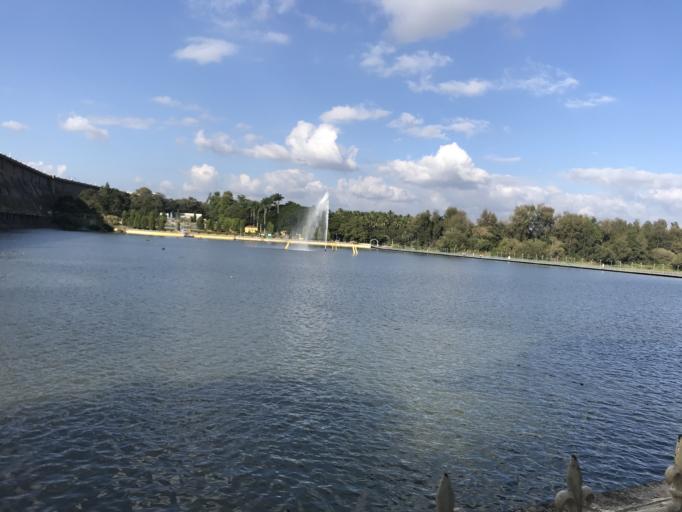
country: IN
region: Karnataka
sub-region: Mandya
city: Shrirangapattana
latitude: 12.4237
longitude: 76.5727
